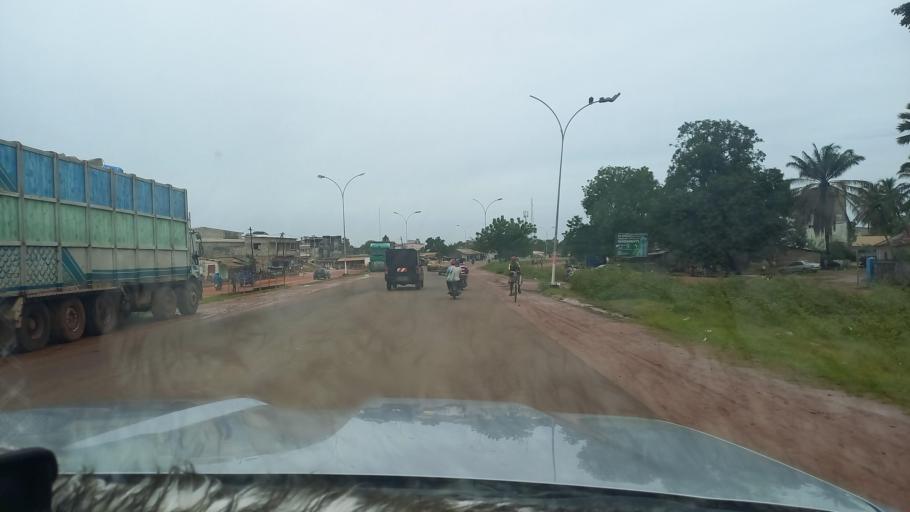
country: SN
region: Ziguinchor
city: Ziguinchor
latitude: 12.5708
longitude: -16.2711
